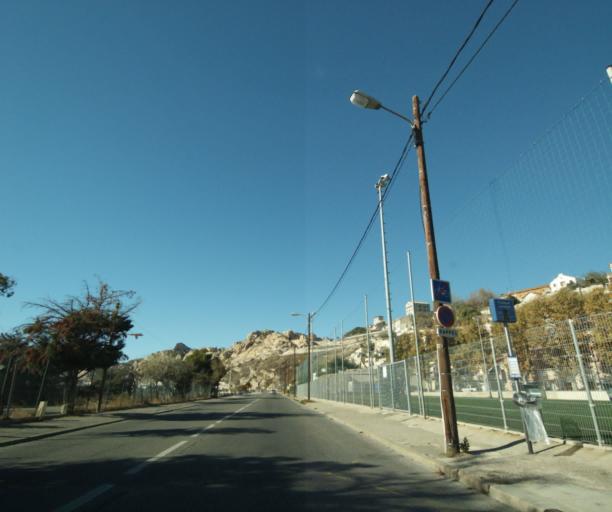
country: FR
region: Provence-Alpes-Cote d'Azur
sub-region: Departement des Bouches-du-Rhone
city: Marseille 16
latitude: 43.3617
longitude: 5.3061
